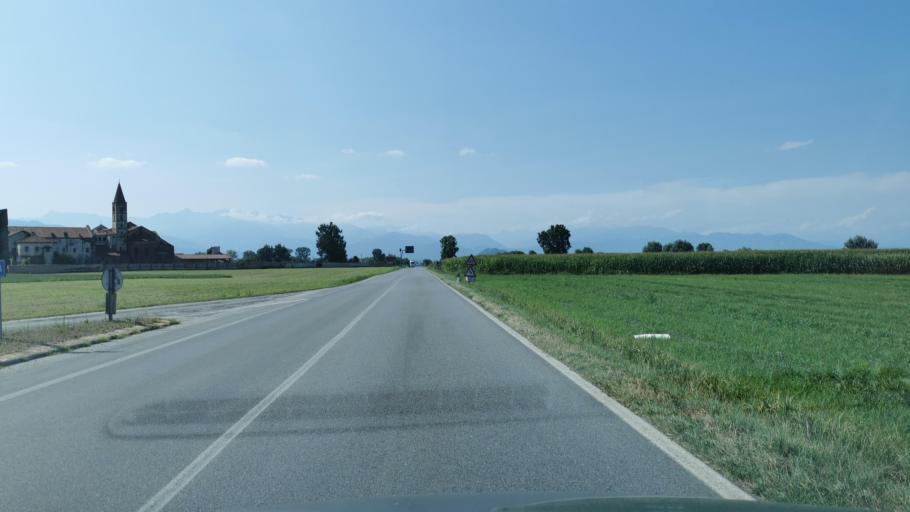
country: IT
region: Piedmont
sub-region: Provincia di Cuneo
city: Carde
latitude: 44.7202
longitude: 7.4413
